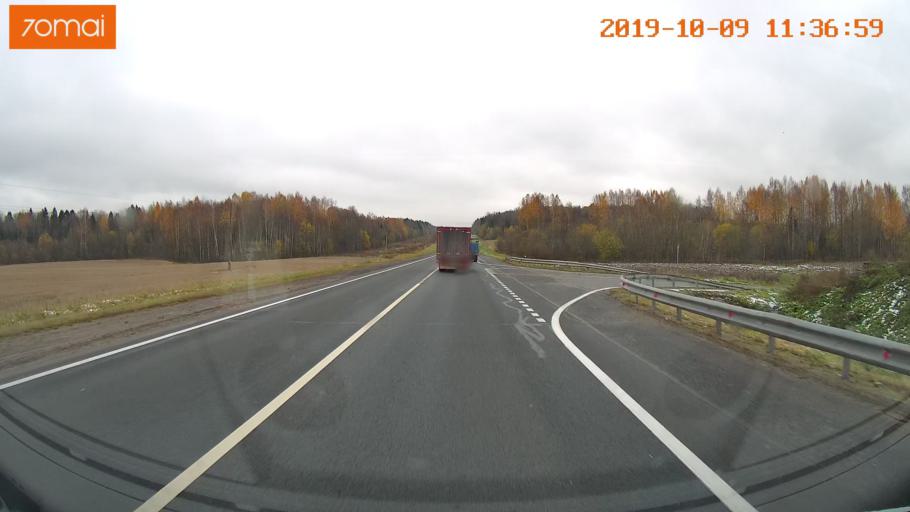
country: RU
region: Vologda
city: Gryazovets
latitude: 58.9840
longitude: 40.1419
